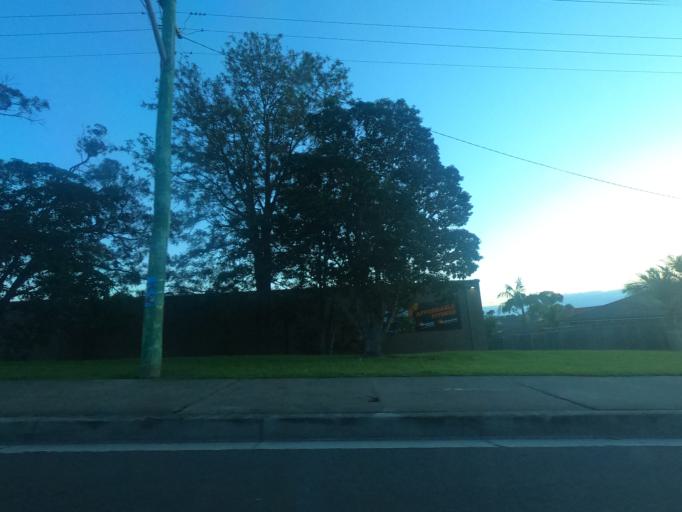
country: AU
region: New South Wales
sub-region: Wollongong
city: Koonawarra
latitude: -34.4933
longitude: 150.8170
